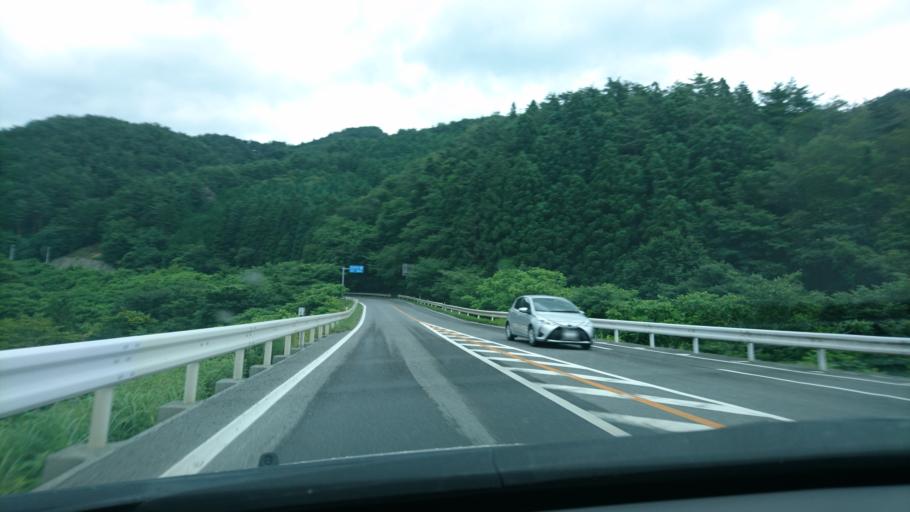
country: JP
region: Iwate
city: Kamaishi
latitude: 39.2122
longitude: 141.8752
